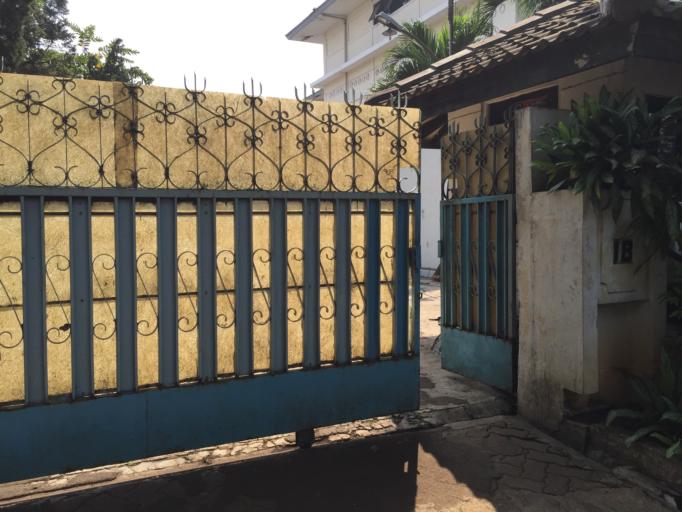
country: ID
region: Jakarta Raya
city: Jakarta
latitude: -6.2046
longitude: 106.8352
